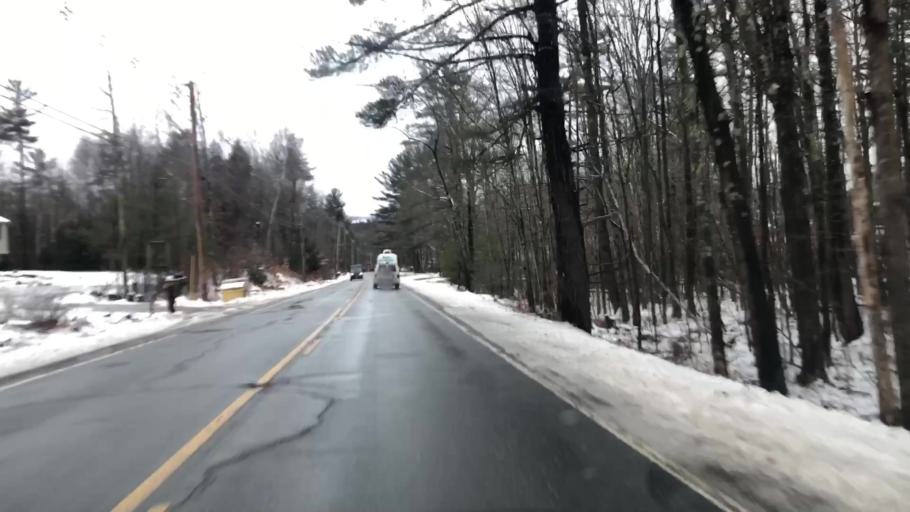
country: US
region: New Hampshire
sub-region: Hillsborough County
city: New Boston
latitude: 43.0142
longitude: -71.6868
